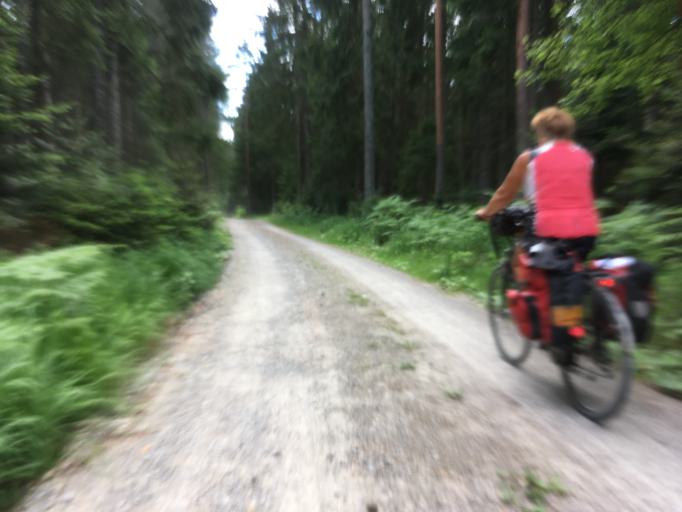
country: DE
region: Baden-Wuerttemberg
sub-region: Karlsruhe Region
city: Baiersbronn
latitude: 48.5494
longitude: 8.4190
